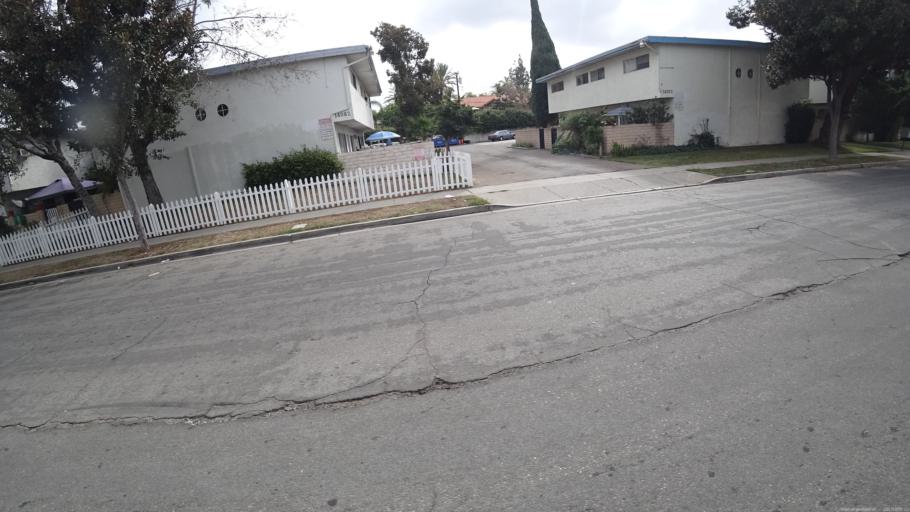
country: US
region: California
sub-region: Orange County
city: Garden Grove
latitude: 33.7586
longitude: -117.9078
